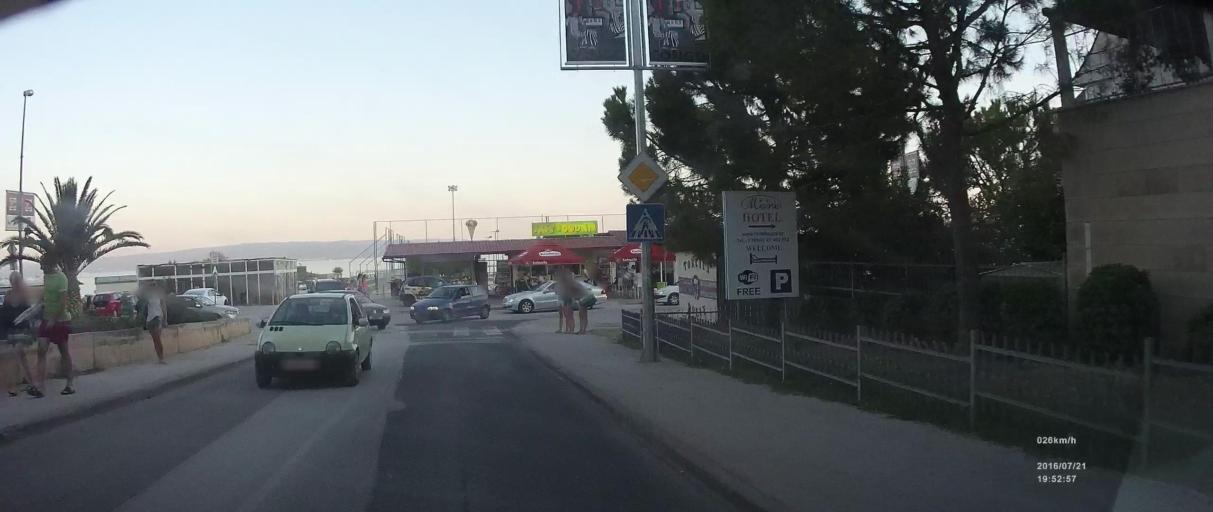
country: HR
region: Splitsko-Dalmatinska
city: Vranjic
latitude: 43.5035
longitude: 16.4763
